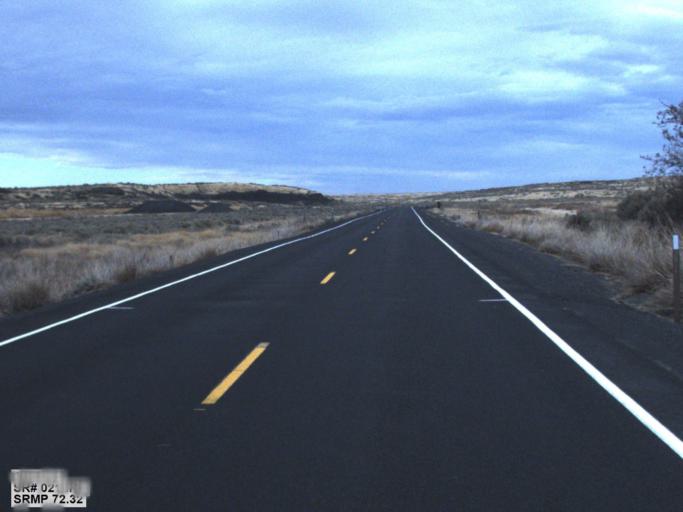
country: US
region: Washington
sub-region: Okanogan County
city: Coulee Dam
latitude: 47.5287
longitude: -118.7829
